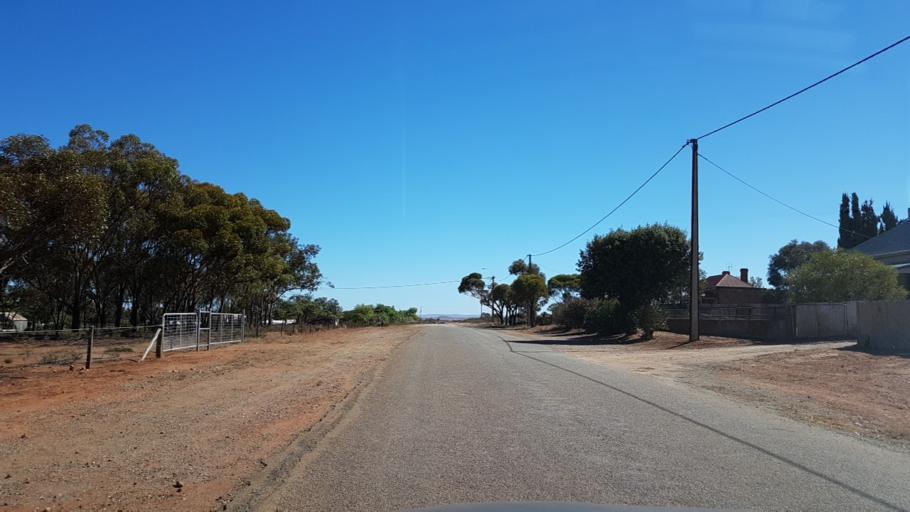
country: AU
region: South Australia
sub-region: Peterborough
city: Peterborough
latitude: -32.9692
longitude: 138.8294
